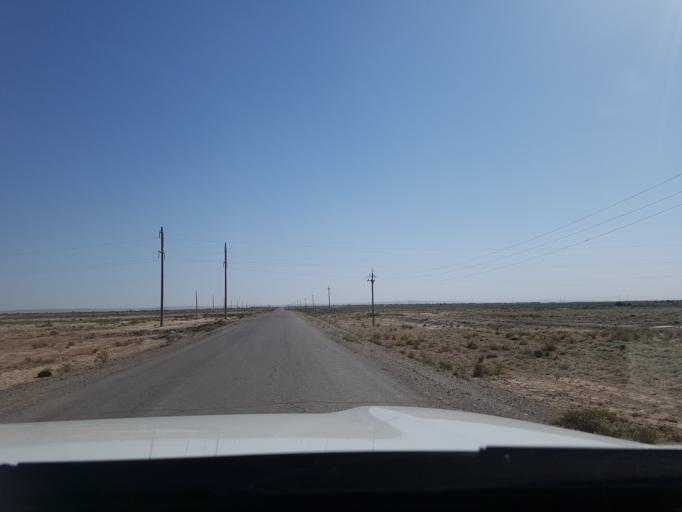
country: IR
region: Razavi Khorasan
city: Sarakhs
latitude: 36.5105
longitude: 61.2532
